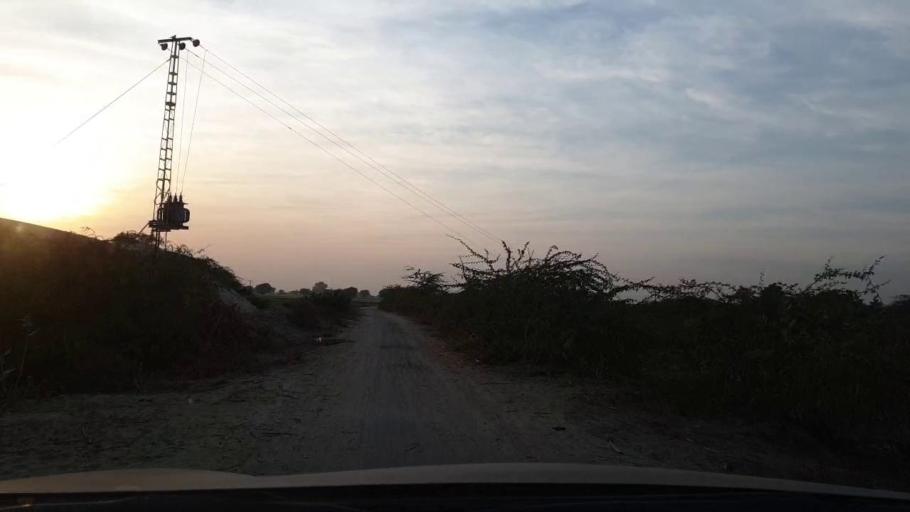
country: PK
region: Sindh
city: Tando Adam
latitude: 25.6770
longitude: 68.7074
